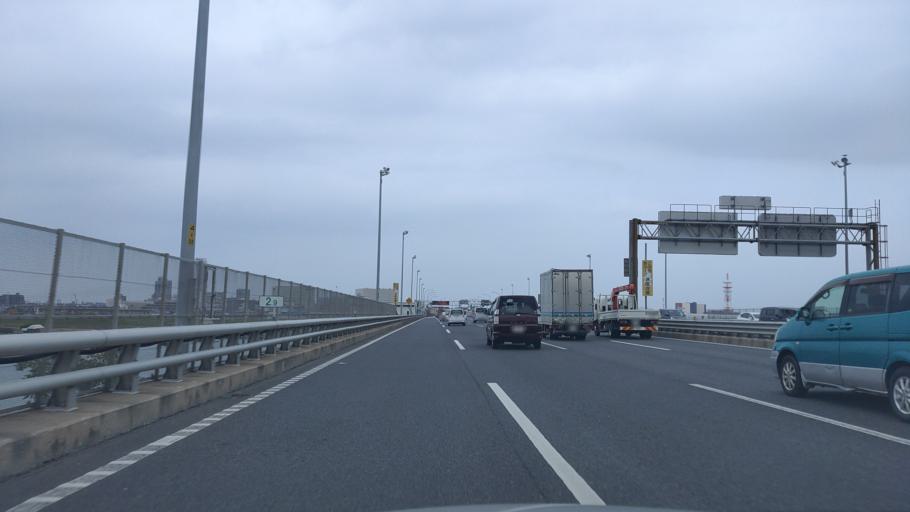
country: JP
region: Tokyo
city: Urayasu
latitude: 35.7084
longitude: 139.9138
